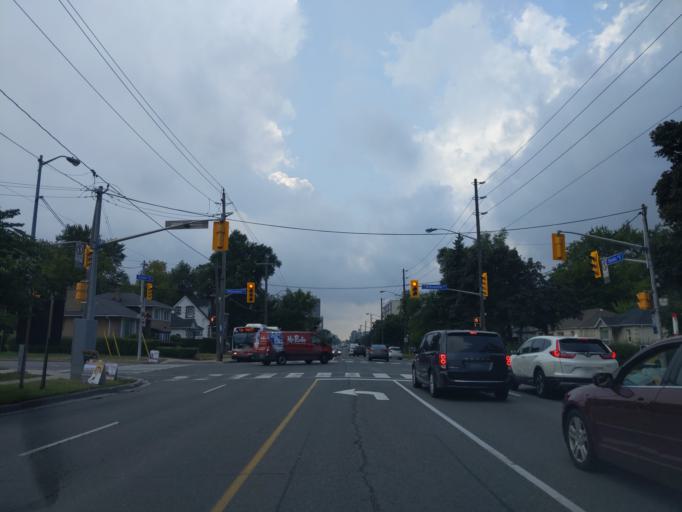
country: CA
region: Ontario
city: North York
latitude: 43.7994
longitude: -79.4141
